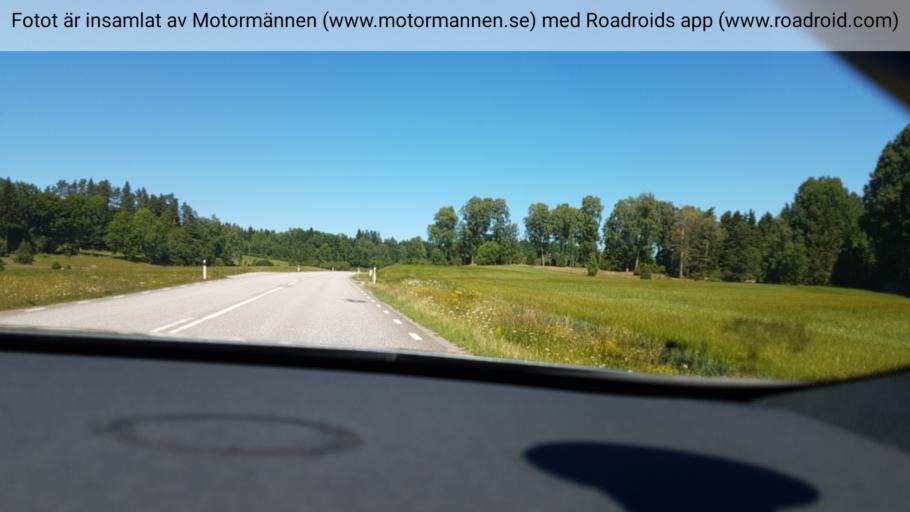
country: SE
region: Vaestra Goetaland
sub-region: Ulricehamns Kommun
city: Ulricehamn
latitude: 57.8797
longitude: 13.4339
